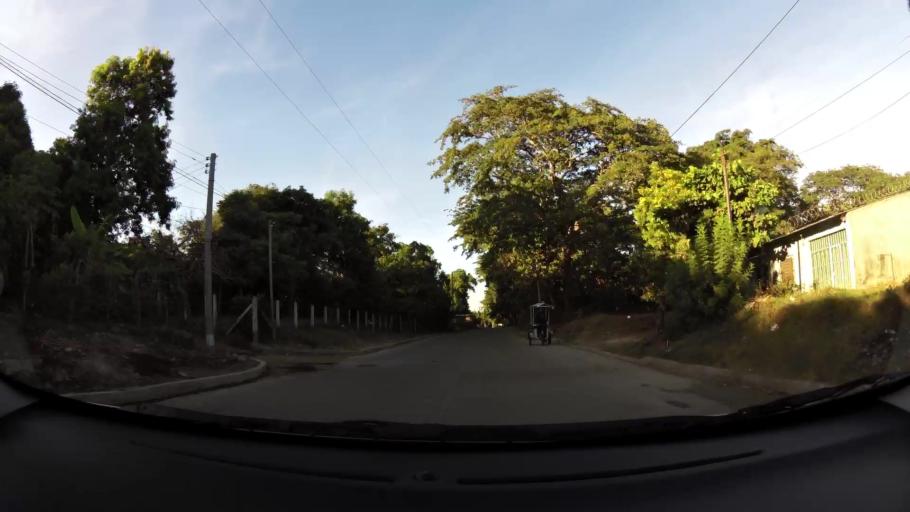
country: SV
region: San Miguel
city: San Miguel
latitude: 13.4595
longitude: -88.1766
